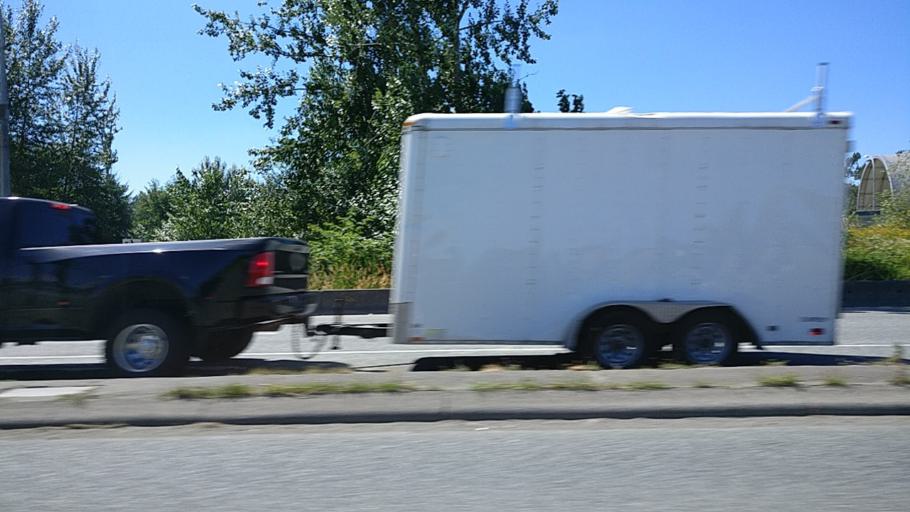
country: CA
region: British Columbia
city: Abbotsford
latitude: 49.0321
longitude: -122.2659
